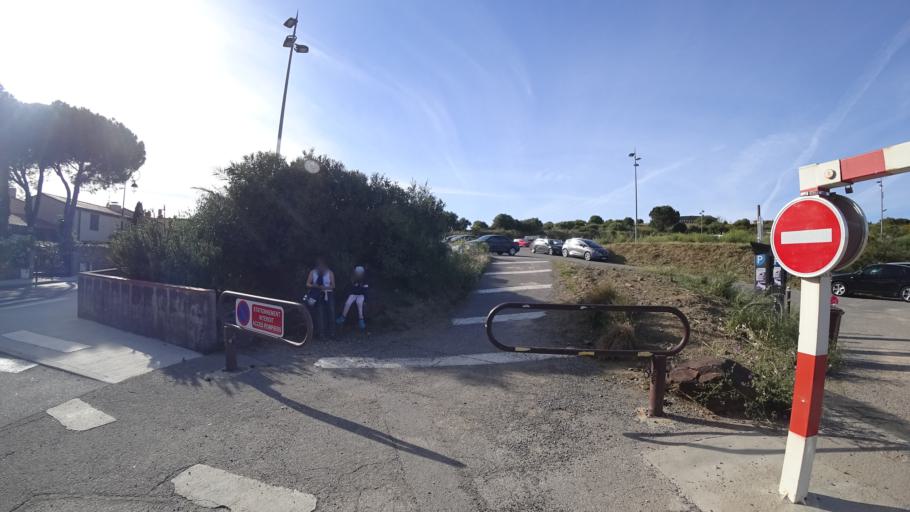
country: FR
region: Languedoc-Roussillon
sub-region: Departement des Pyrenees-Orientales
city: Collioure
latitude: 42.5296
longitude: 3.0792
